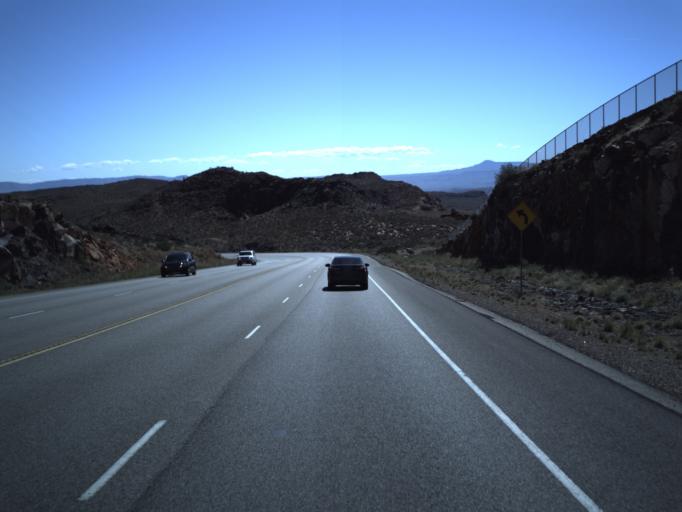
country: US
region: Utah
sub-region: Washington County
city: Santa Clara
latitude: 37.1634
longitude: -113.6112
